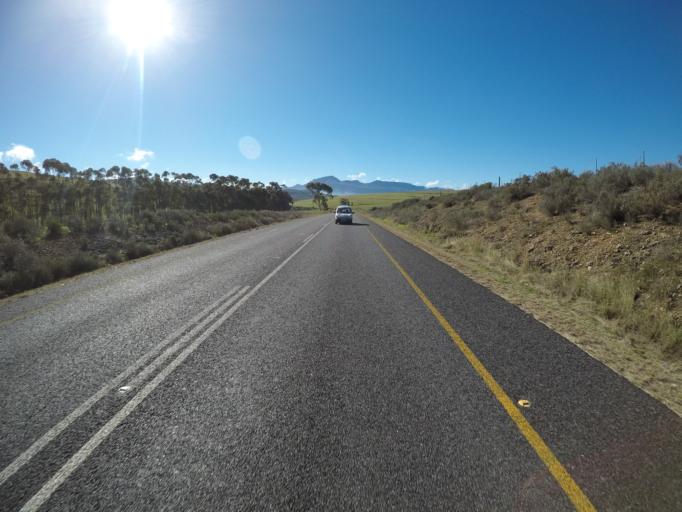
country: ZA
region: Western Cape
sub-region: Overberg District Municipality
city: Caledon
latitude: -34.1144
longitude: 19.5222
